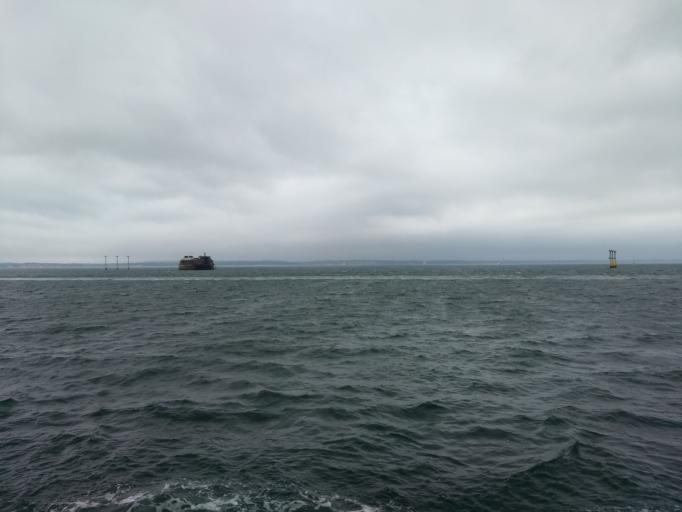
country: GB
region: England
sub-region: Portsmouth
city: Southsea
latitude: 50.7767
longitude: -1.0945
